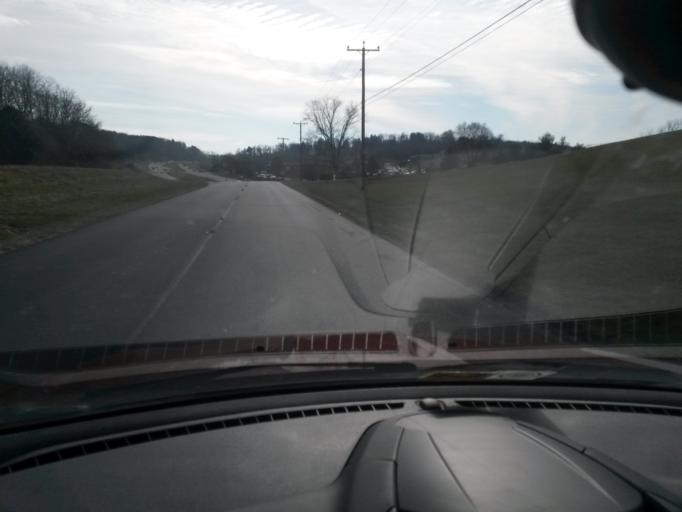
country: US
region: Virginia
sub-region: Botetourt County
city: Daleville
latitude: 37.3996
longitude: -79.9109
